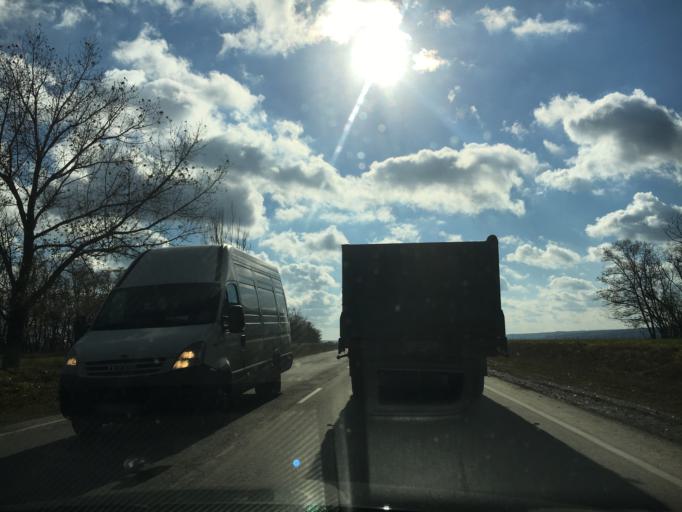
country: RU
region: Rostov
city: Matveyev Kurgan
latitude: 47.5410
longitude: 38.8914
